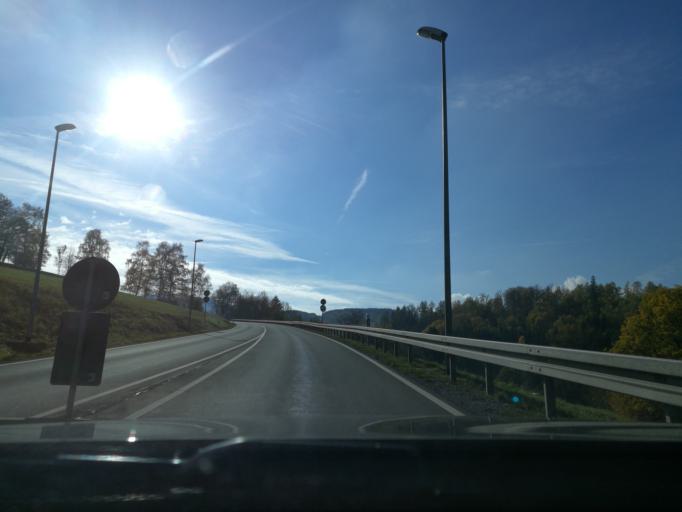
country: DE
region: Hesse
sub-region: Regierungsbezirk Kassel
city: Gersfeld
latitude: 50.4425
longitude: 9.9176
